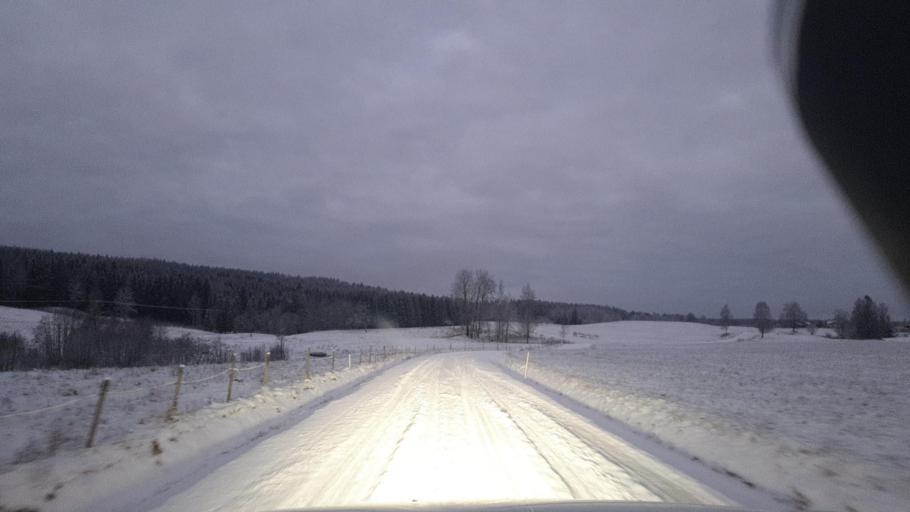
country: SE
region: Vaermland
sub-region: Eda Kommun
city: Amotfors
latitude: 59.7185
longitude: 12.1461
